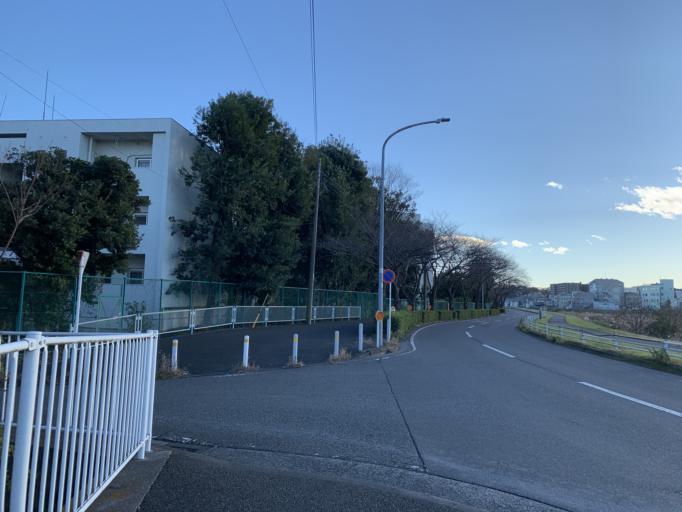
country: JP
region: Tokyo
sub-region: Machida-shi
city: Machida
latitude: 35.5176
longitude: 139.5522
